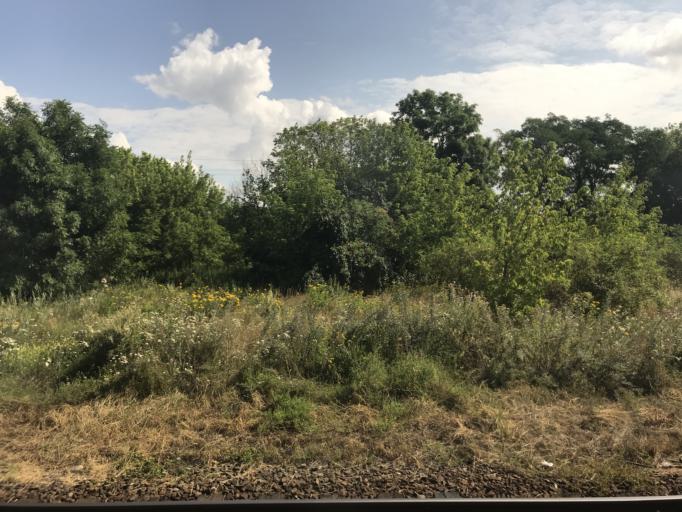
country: PL
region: Kujawsko-Pomorskie
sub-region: Powiat inowroclawski
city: Zlotniki Kujawskie
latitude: 52.9042
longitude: 18.1469
